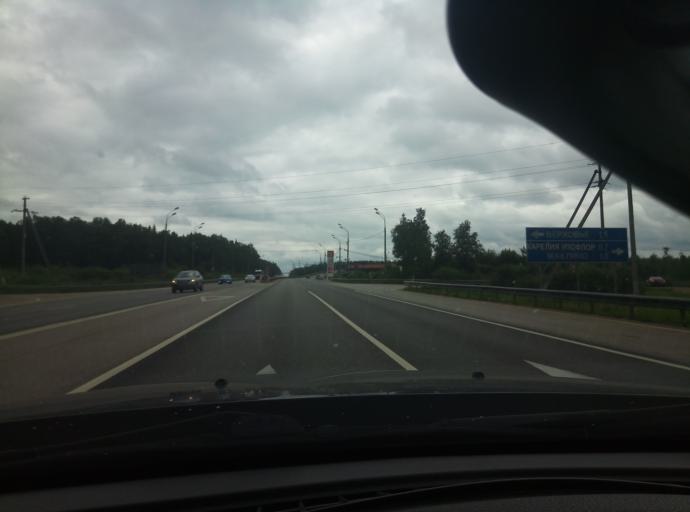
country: RU
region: Kaluga
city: Maloyaroslavets
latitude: 54.9835
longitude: 36.5002
